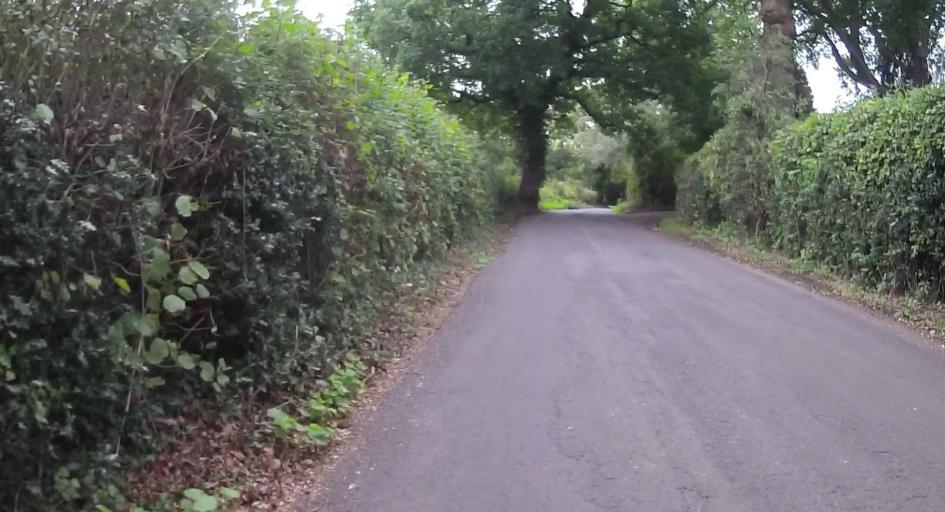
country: GB
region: England
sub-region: Surrey
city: Knaphill
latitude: 51.3285
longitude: -0.6291
